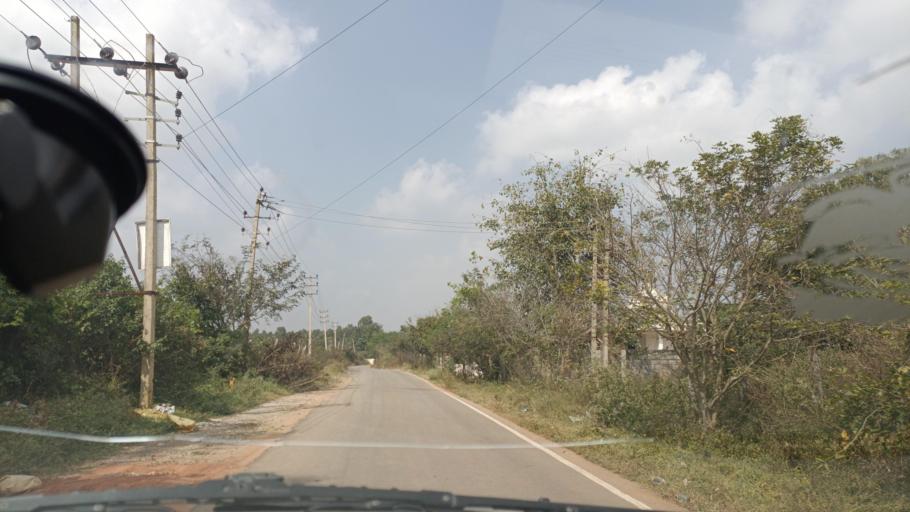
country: IN
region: Karnataka
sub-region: Bangalore Urban
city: Yelahanka
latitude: 13.1498
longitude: 77.6349
